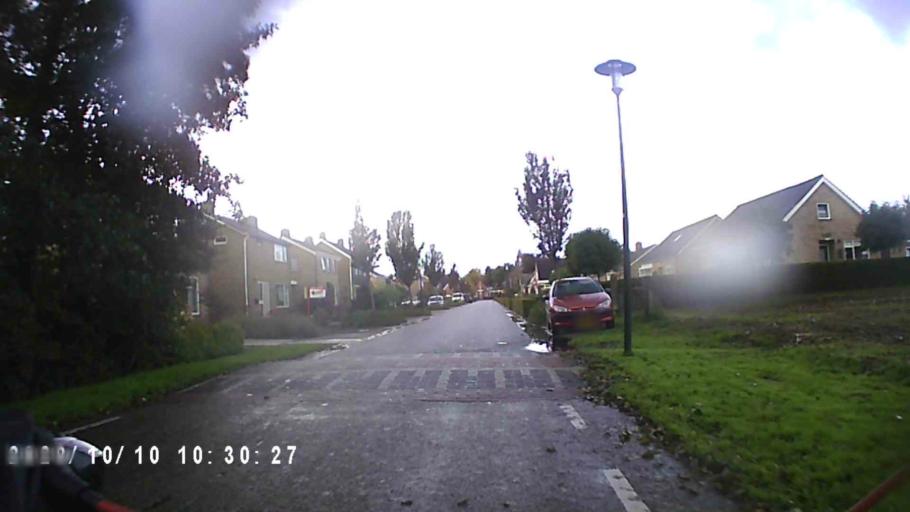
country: NL
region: Groningen
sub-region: Gemeente Leek
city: Leek
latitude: 53.1870
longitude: 6.3327
